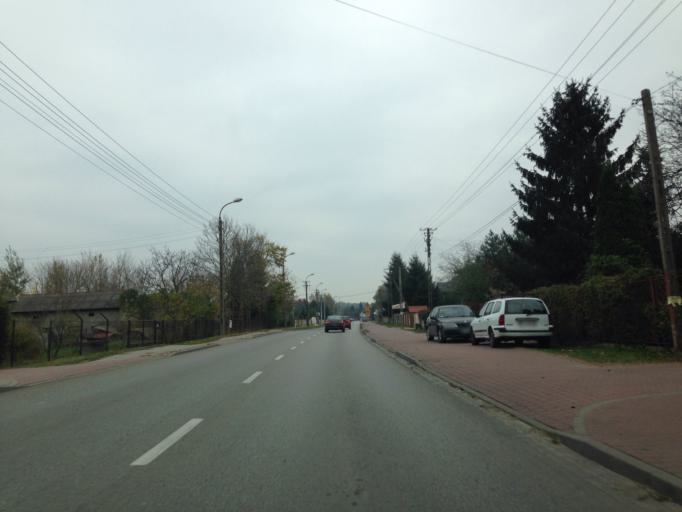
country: PL
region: Masovian Voivodeship
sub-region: Powiat warszawski zachodni
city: Stare Babice
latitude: 52.2535
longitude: 20.8019
